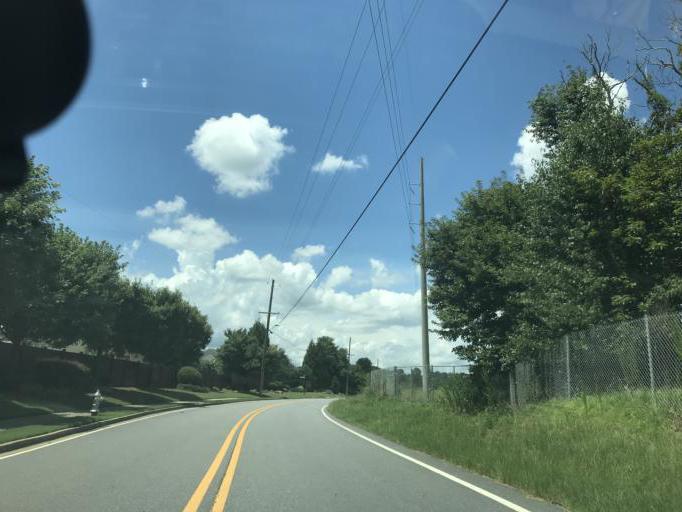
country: US
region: Georgia
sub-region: Gwinnett County
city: Suwanee
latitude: 34.0546
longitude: -84.1170
